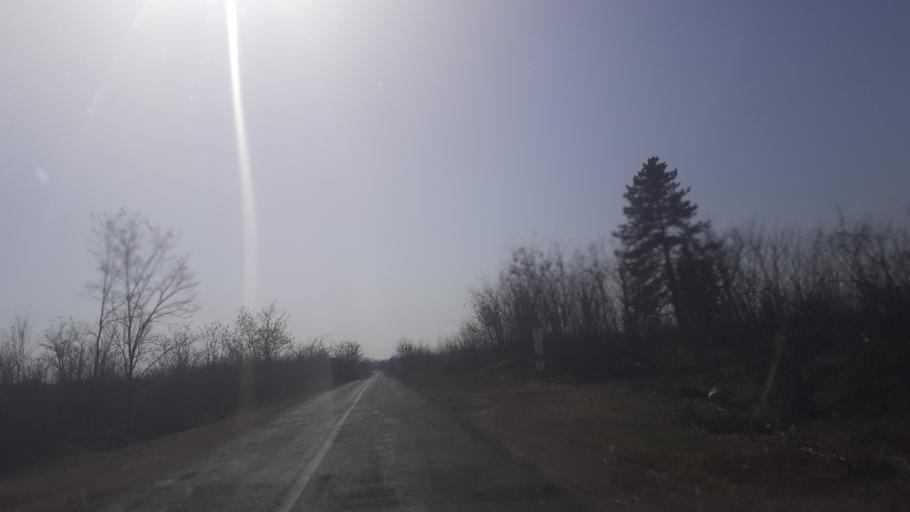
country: HU
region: Pest
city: Dabas
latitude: 47.1462
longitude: 19.3288
